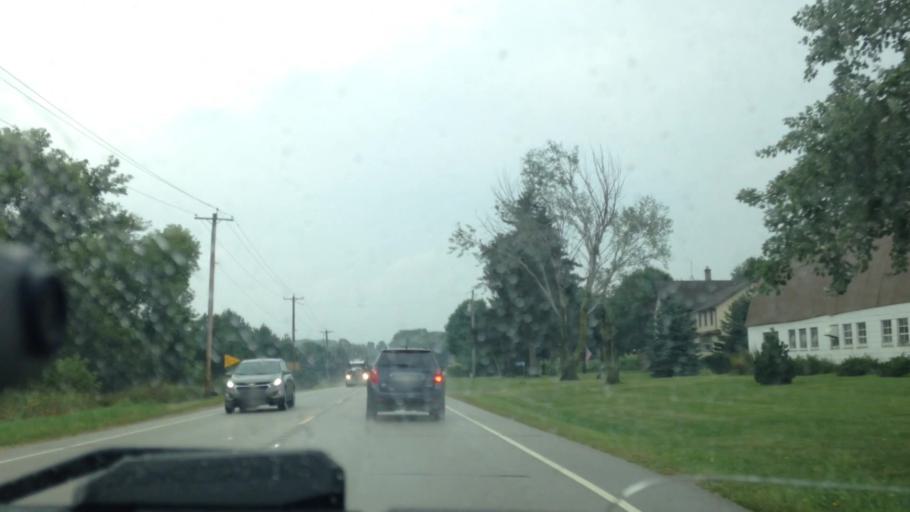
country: US
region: Wisconsin
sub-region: Washington County
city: Hartford
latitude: 43.3879
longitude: -88.3552
